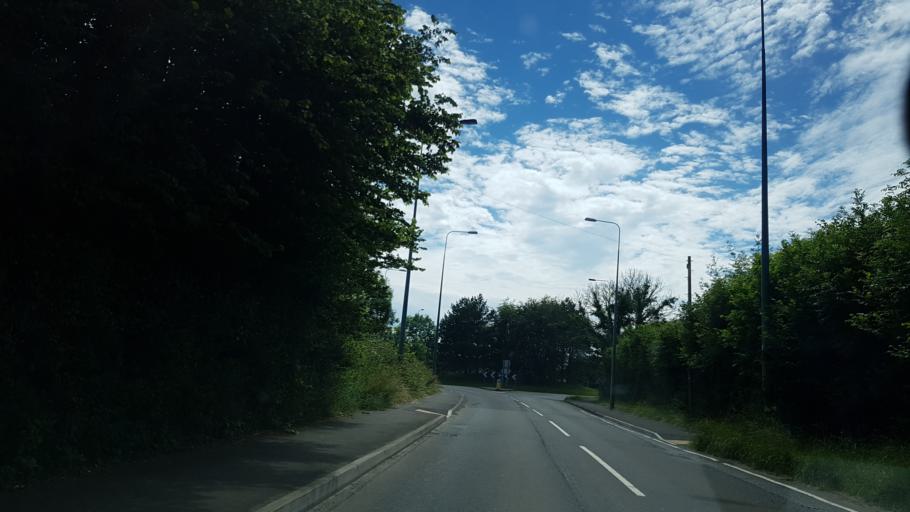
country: GB
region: Wales
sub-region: Pembrokeshire
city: Haverfordwest
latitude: 51.8169
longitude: -4.9562
